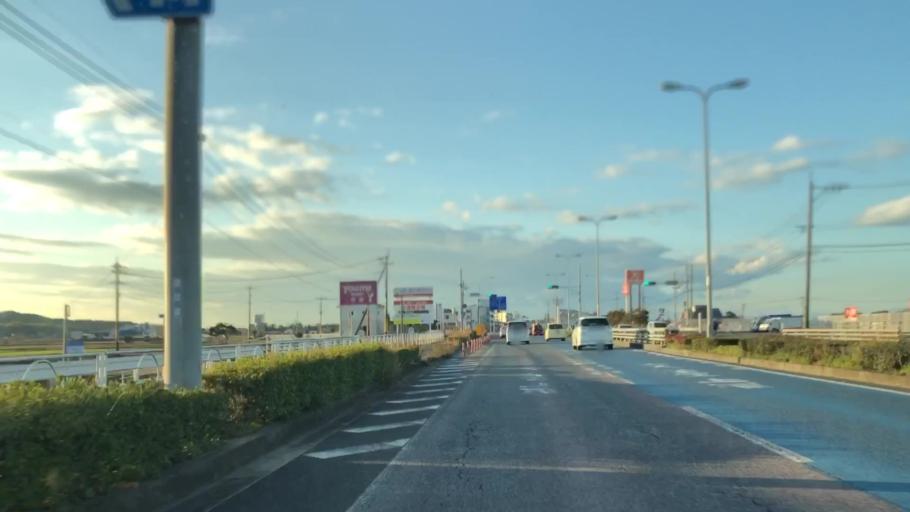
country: JP
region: Fukuoka
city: Nakatsu
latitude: 33.5497
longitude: 131.2762
